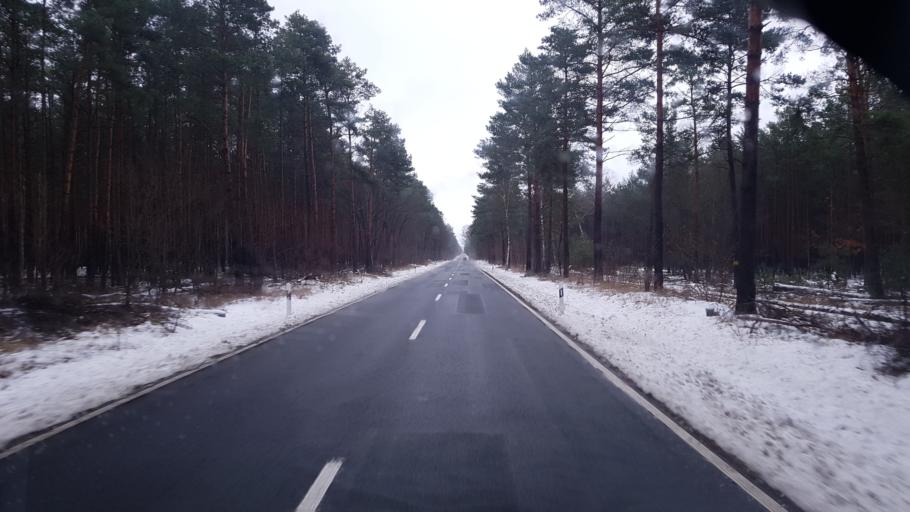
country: DE
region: Brandenburg
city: Tauer
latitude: 51.9818
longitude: 14.4563
